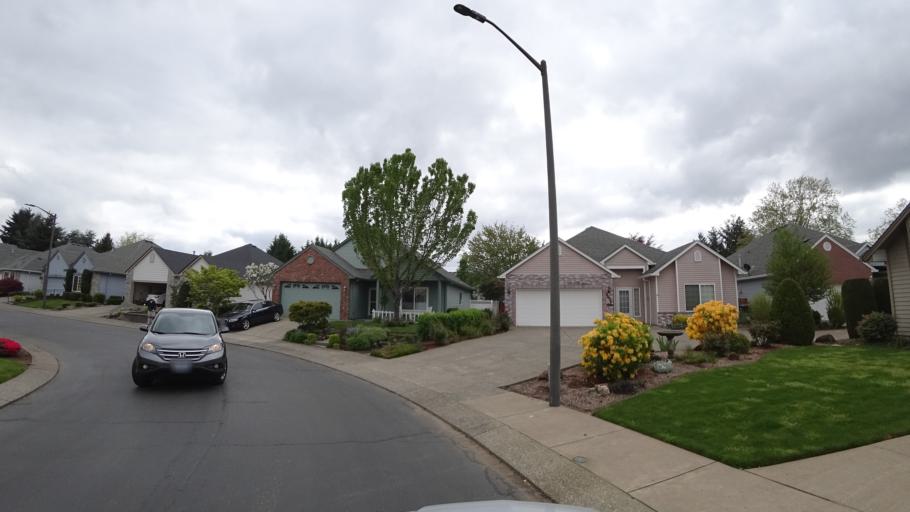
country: US
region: Oregon
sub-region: Washington County
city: Hillsboro
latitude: 45.5388
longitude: -122.9782
